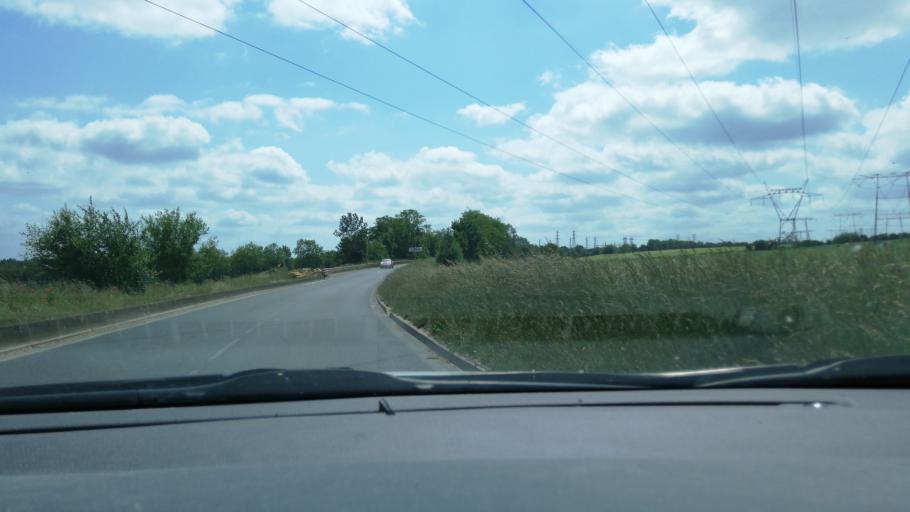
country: FR
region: Ile-de-France
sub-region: Departement du Val-d'Oise
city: Vaureal
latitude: 49.0633
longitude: 2.0212
